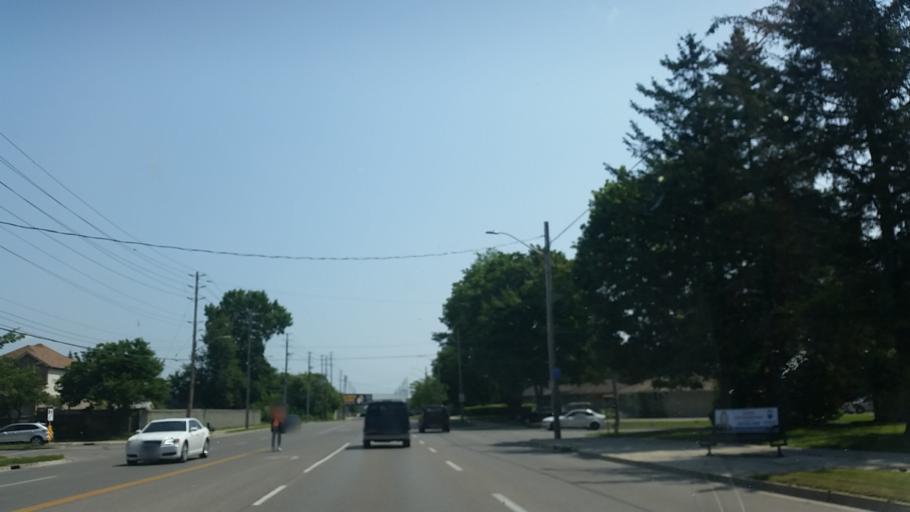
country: CA
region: Ontario
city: London
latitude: 42.9812
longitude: -81.3014
